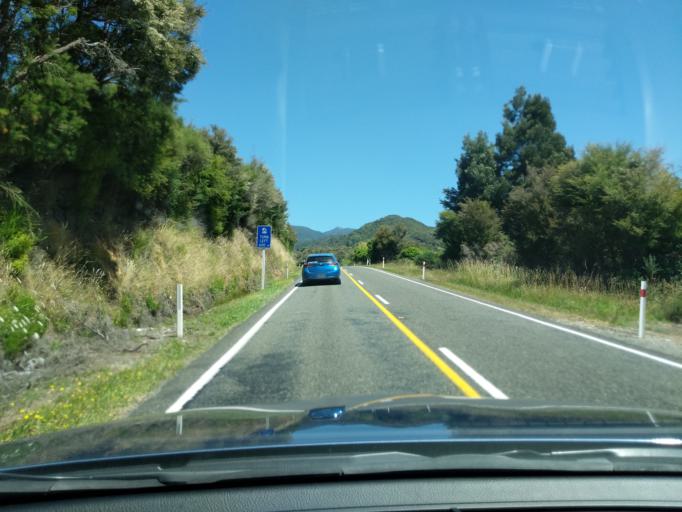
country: NZ
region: Tasman
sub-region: Tasman District
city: Takaka
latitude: -40.7392
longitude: 172.6913
